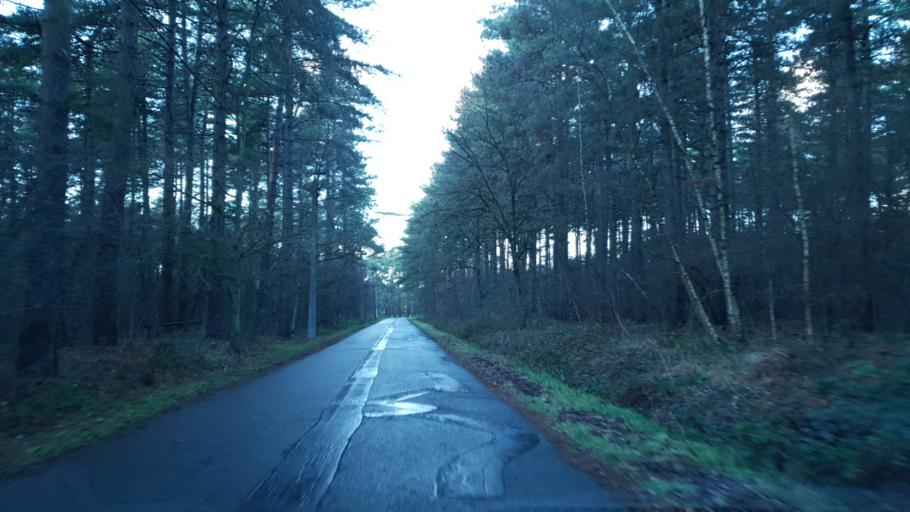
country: BE
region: Flanders
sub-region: Provincie Antwerpen
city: Stabroek
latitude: 51.3541
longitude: 4.3604
